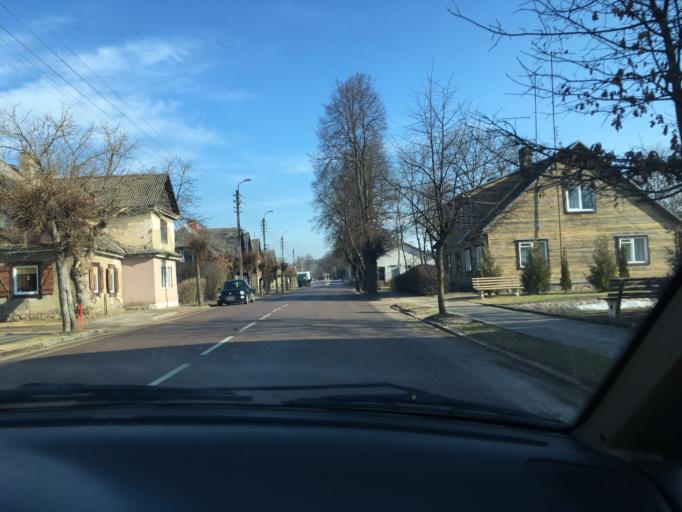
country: LT
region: Panevezys
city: Rokiskis
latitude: 55.7452
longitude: 25.8383
